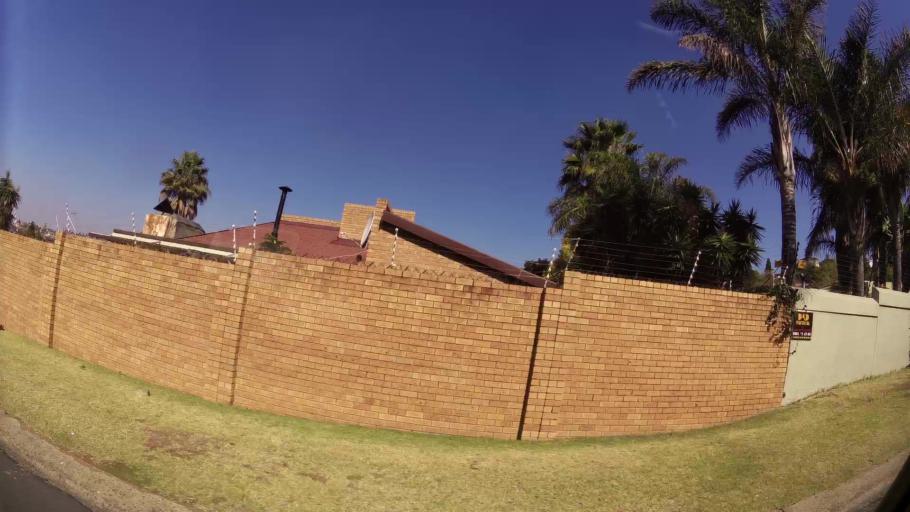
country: ZA
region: Gauteng
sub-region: City of Johannesburg Metropolitan Municipality
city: Johannesburg
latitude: -26.2641
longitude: 28.0448
